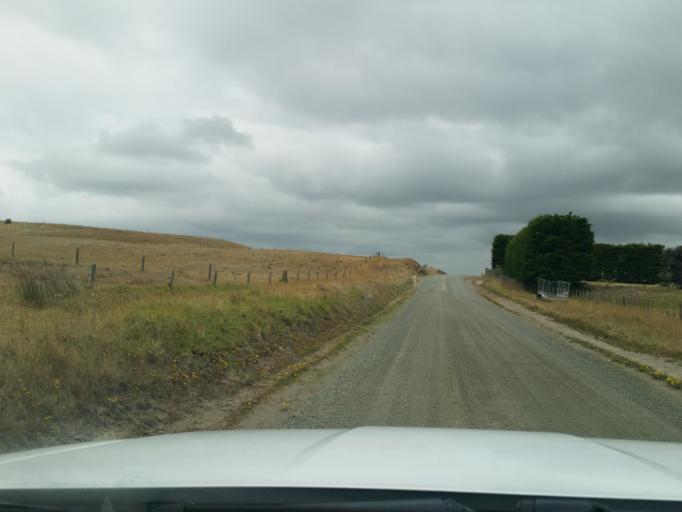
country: NZ
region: Northland
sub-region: Kaipara District
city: Dargaville
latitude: -35.9898
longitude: 173.8274
